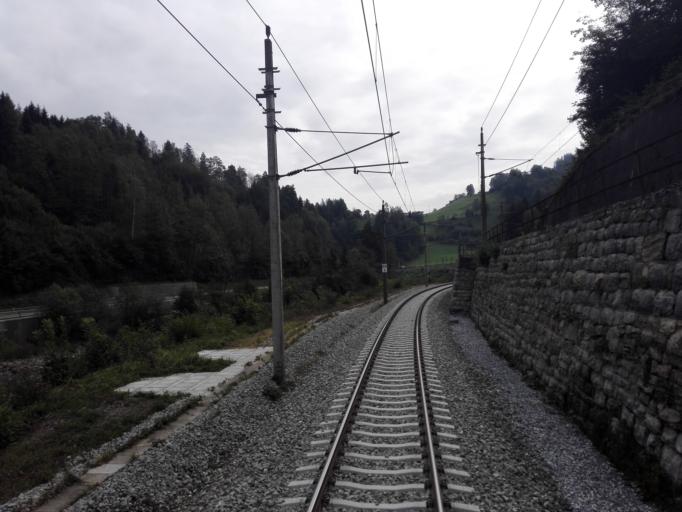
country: AT
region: Salzburg
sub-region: Politischer Bezirk Sankt Johann im Pongau
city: Goldegg
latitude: 47.3098
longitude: 13.1223
